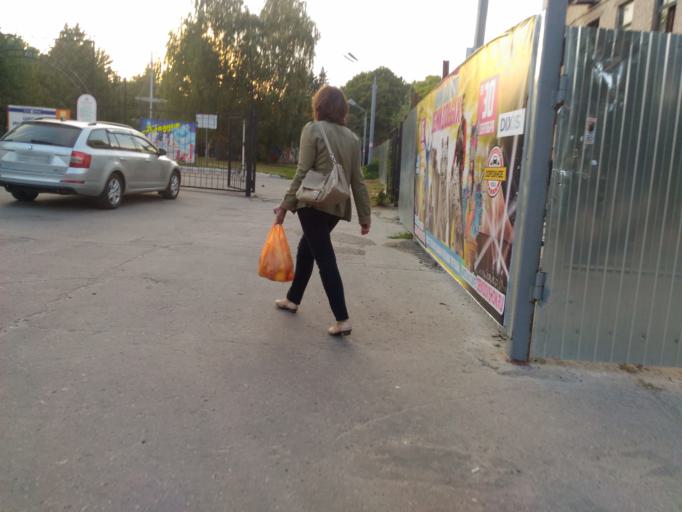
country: RU
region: Ulyanovsk
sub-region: Ulyanovskiy Rayon
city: Ulyanovsk
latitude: 54.3033
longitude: 48.3289
